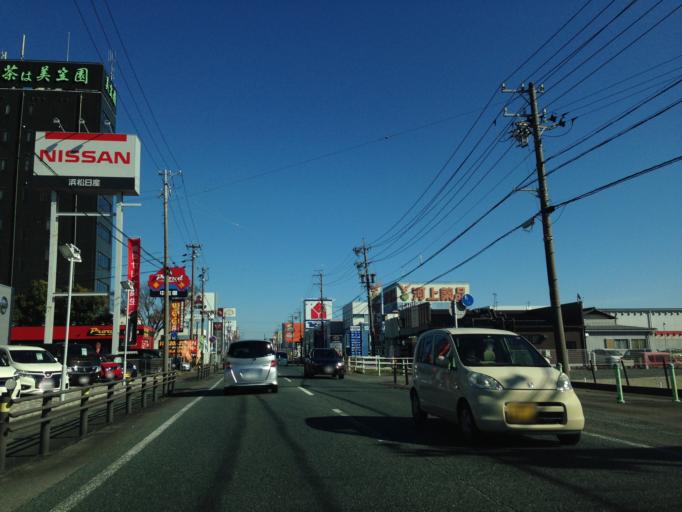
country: JP
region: Shizuoka
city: Kakegawa
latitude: 34.7724
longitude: 137.9828
